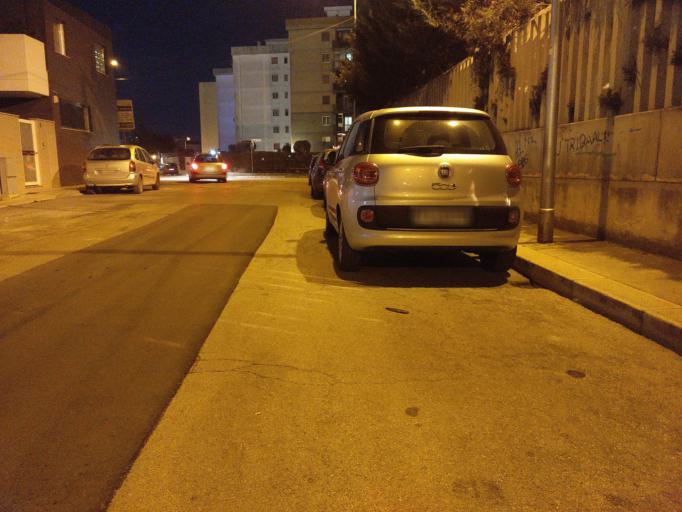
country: IT
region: Apulia
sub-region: Provincia di Bari
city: Modugno
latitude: 41.0815
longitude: 16.7886
